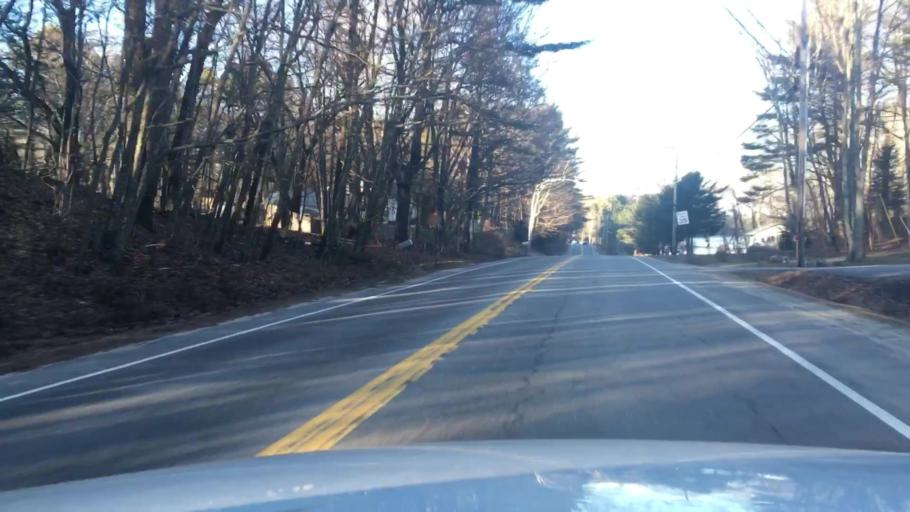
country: US
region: Maine
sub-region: Cumberland County
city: Brunswick
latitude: 43.8517
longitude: -69.9129
